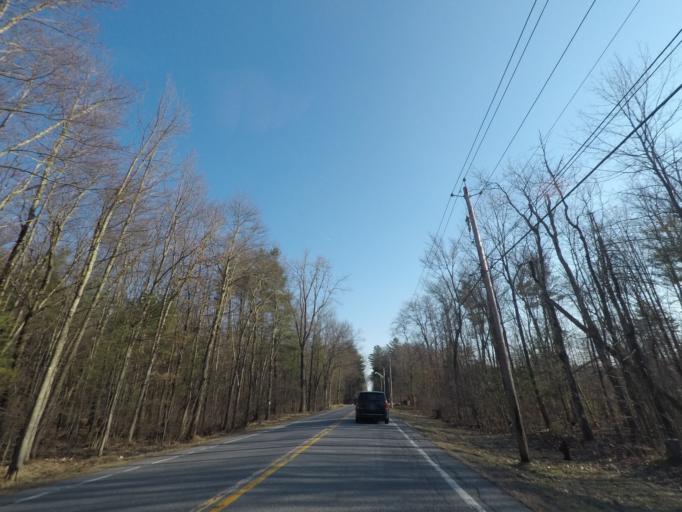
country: US
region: New York
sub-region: Schenectady County
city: Niskayuna
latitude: 42.8279
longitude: -73.7756
